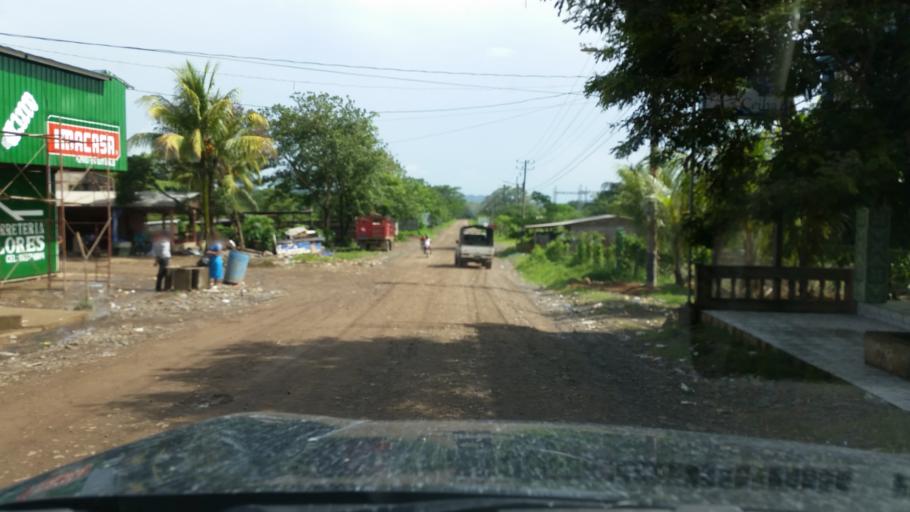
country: NI
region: Atlantico Norte (RAAN)
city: Siuna
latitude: 13.7124
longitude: -84.7749
